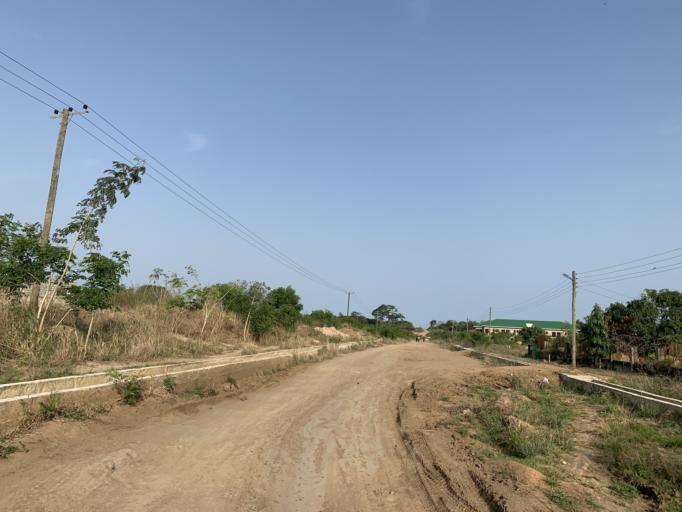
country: GH
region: Central
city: Winneba
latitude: 5.3810
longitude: -0.6211
